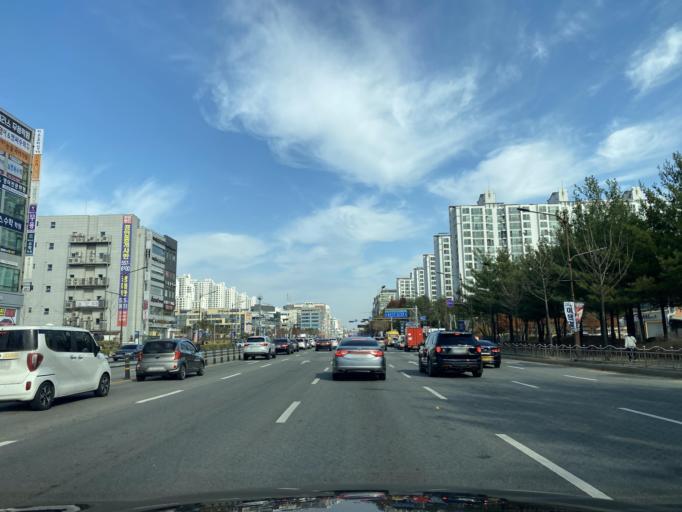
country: KR
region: Chungcheongnam-do
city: Cheonan
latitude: 36.8063
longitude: 127.1069
